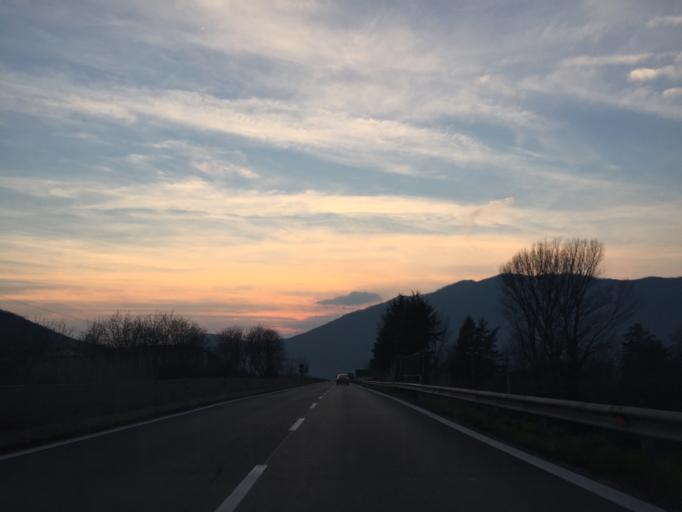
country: IT
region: Campania
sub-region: Provincia di Avellino
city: San Pietro
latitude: 40.8174
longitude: 14.7897
